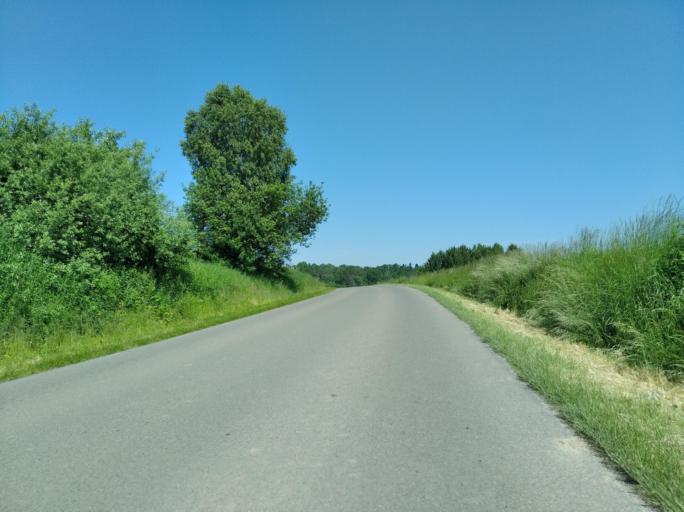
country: PL
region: Subcarpathian Voivodeship
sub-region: Powiat ropczycko-sedziszowski
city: Wielopole Skrzynskie
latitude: 49.9548
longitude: 21.6168
